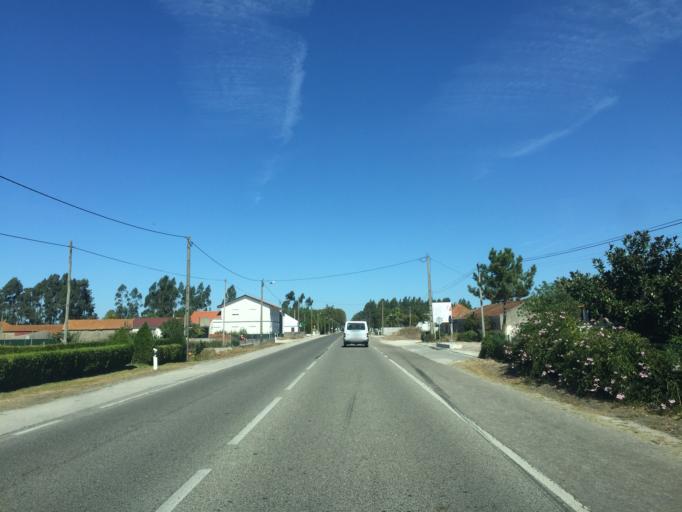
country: PT
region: Coimbra
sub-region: Figueira da Foz
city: Alhadas
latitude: 40.2719
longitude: -8.7763
